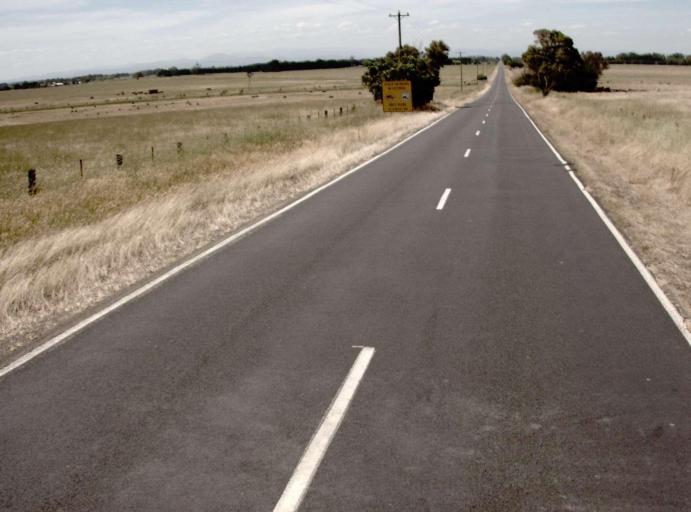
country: AU
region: Victoria
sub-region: Wellington
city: Heyfield
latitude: -38.1118
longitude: 146.8619
